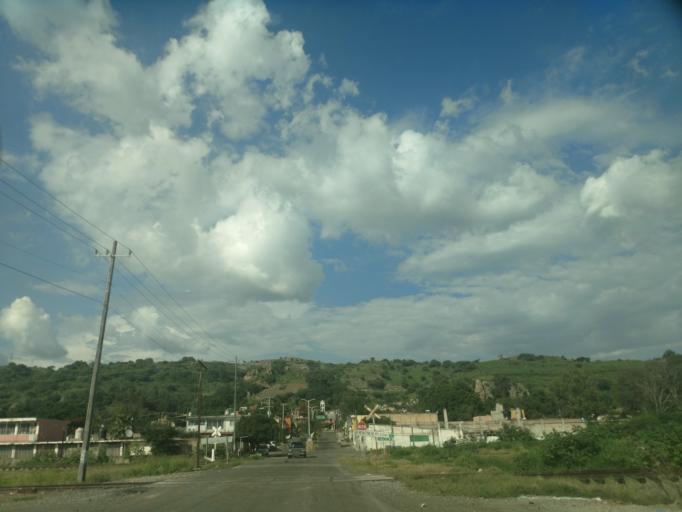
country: MX
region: Jalisco
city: Antonio Escobedo
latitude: 20.9097
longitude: -103.9903
